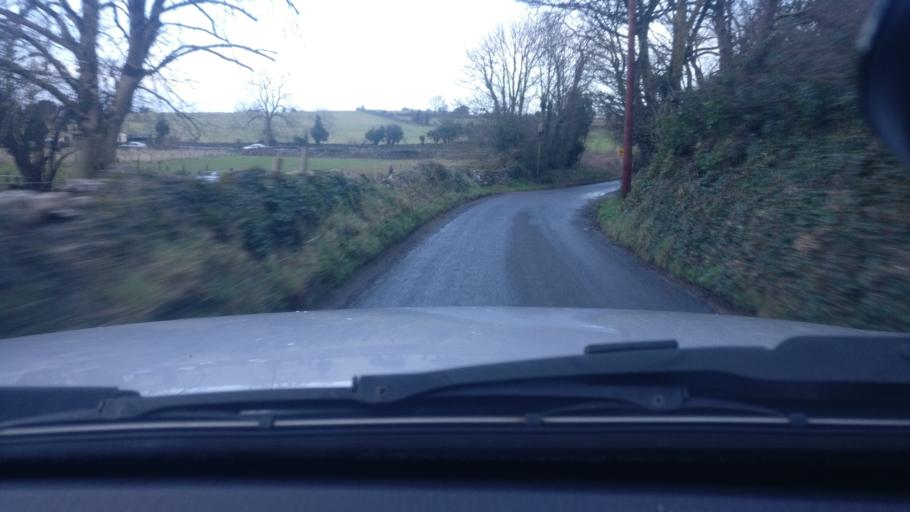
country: IE
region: Connaught
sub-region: County Galway
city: Loughrea
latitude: 53.1886
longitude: -8.6021
